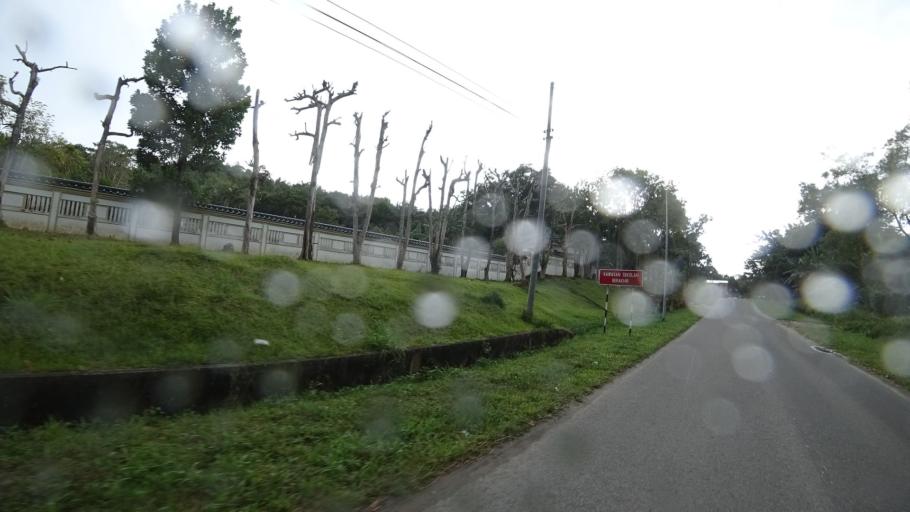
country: BN
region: Brunei and Muara
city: Bandar Seri Begawan
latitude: 4.8649
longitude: 114.9449
